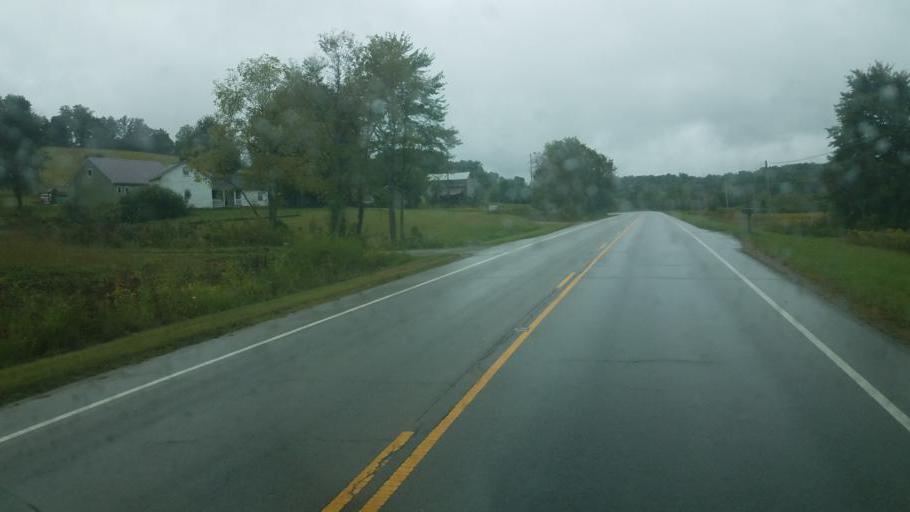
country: US
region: Ohio
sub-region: Jackson County
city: Oak Hill
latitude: 38.8740
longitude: -82.5904
